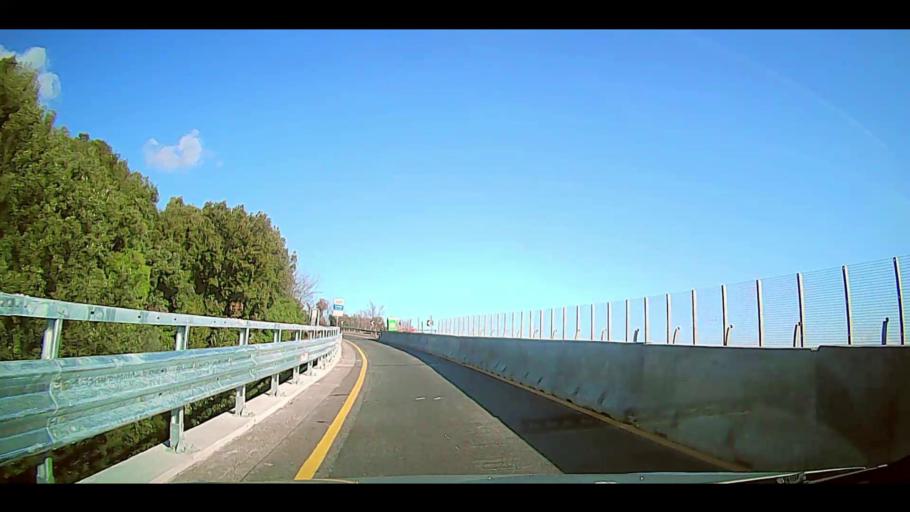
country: IT
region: Calabria
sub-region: Provincia di Crotone
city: Caccuri
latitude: 39.2254
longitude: 16.7956
